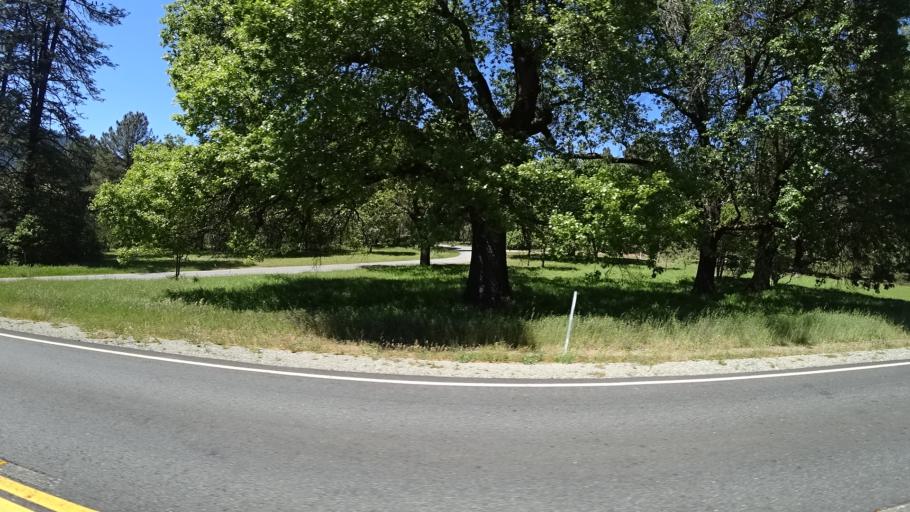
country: US
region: California
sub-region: Trinity County
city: Weaverville
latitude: 40.7267
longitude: -123.0440
